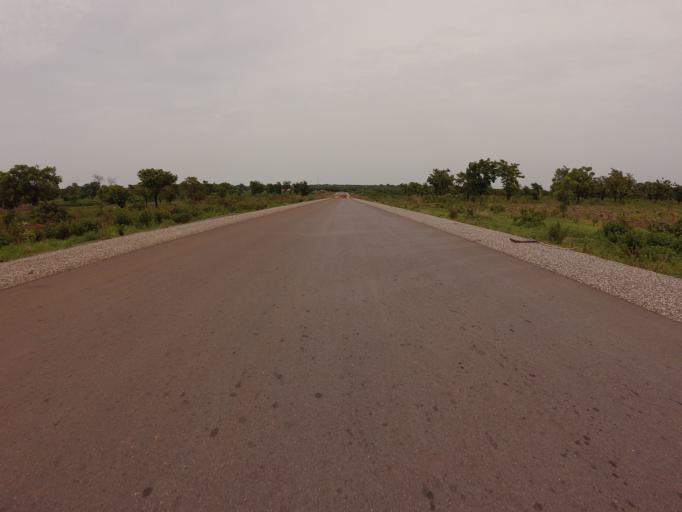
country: GH
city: Kpandae
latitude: 8.9400
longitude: -0.0173
